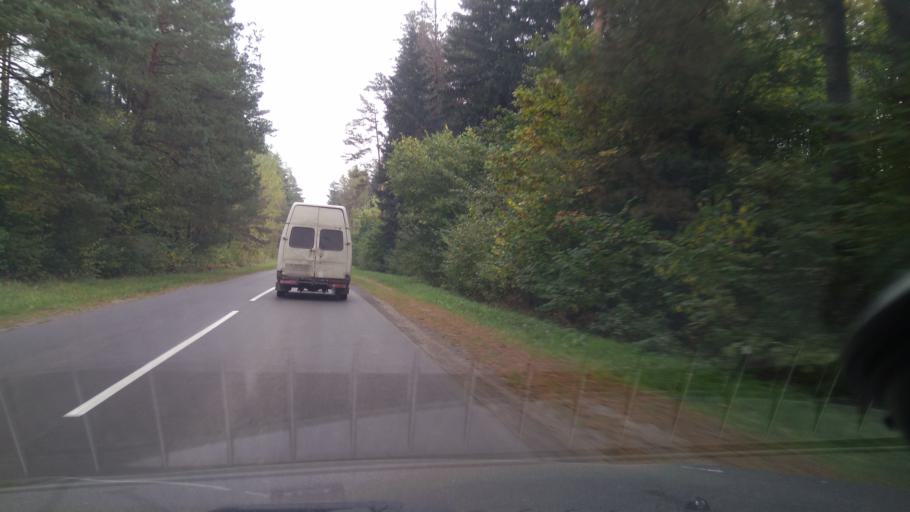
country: BY
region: Minsk
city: Rudzyensk
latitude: 53.6135
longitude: 27.7824
